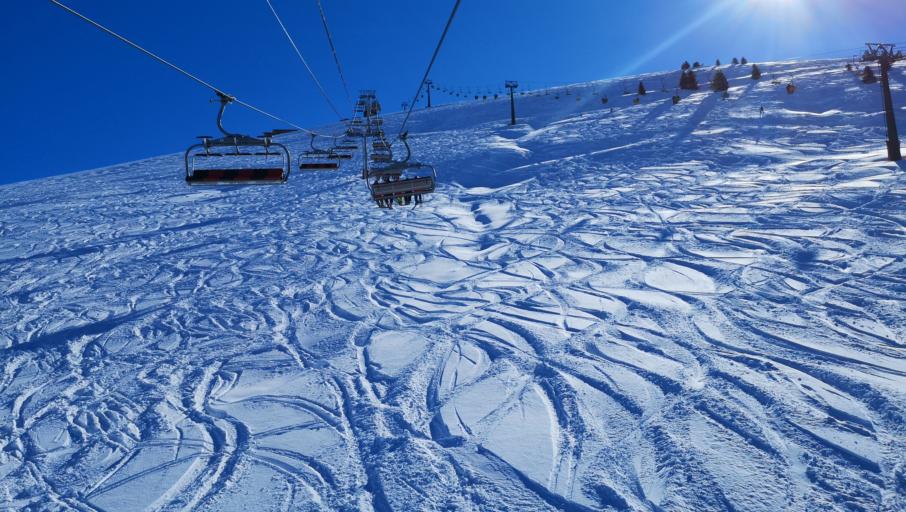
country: FR
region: Rhone-Alpes
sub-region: Departement de la Haute-Savoie
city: Megeve
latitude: 45.8474
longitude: 6.6703
